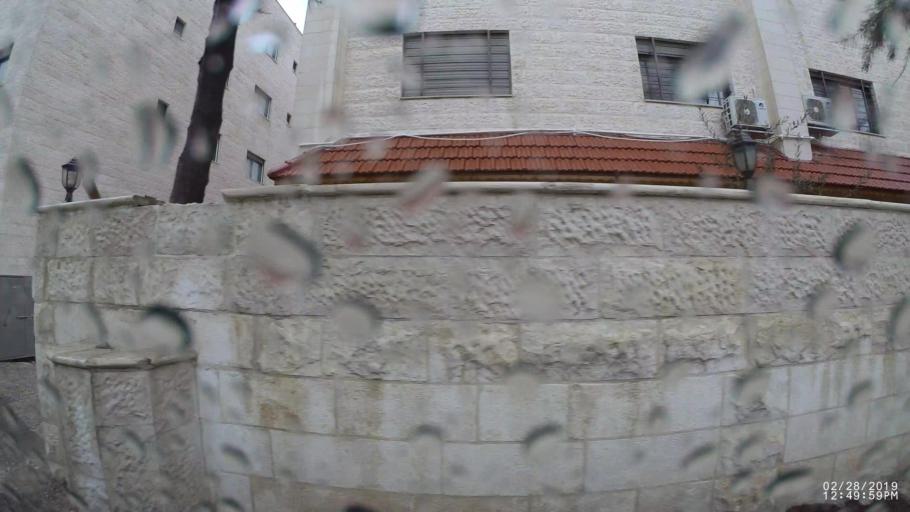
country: JO
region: Amman
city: Al Jubayhah
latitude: 32.0256
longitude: 35.8835
